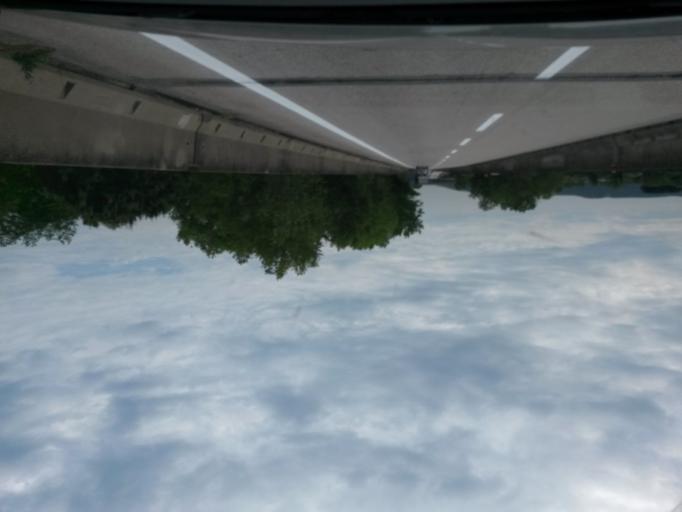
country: IT
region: Tuscany
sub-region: Provincia di Livorno
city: Donoratico
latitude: 43.1818
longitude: 10.5653
